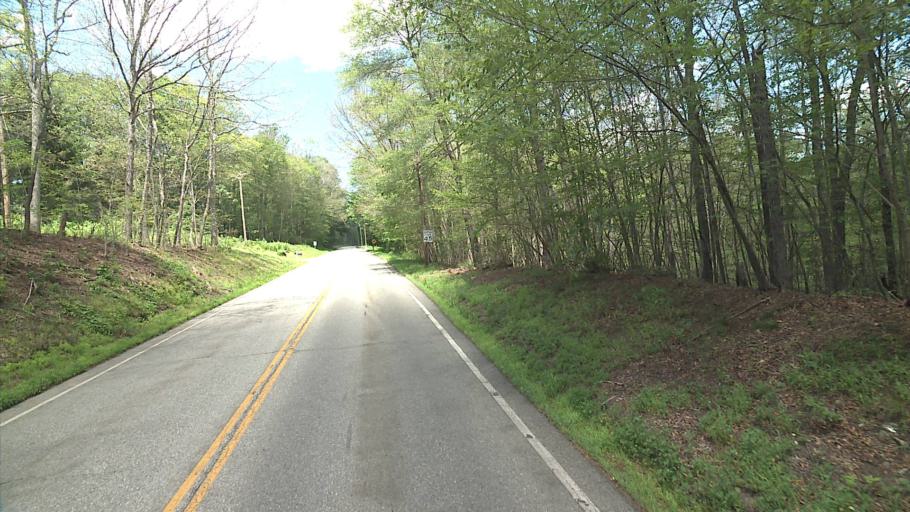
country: US
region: Connecticut
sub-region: Middlesex County
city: East Hampton
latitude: 41.5365
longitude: -72.4978
